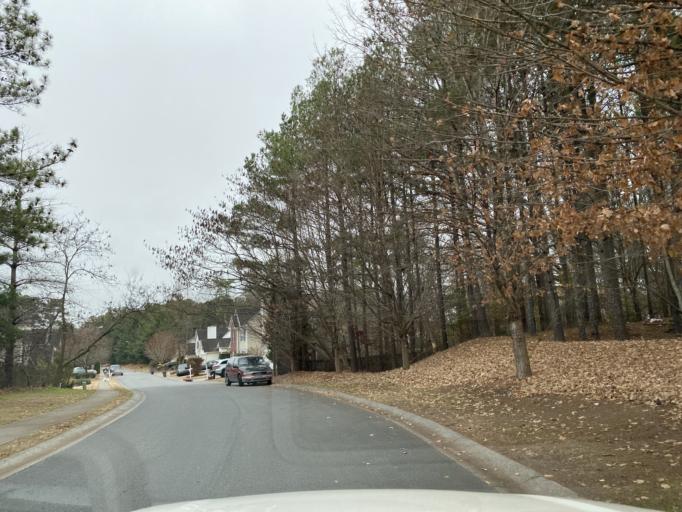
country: US
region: Georgia
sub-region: Cobb County
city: Fair Oaks
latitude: 33.9209
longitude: -84.5780
